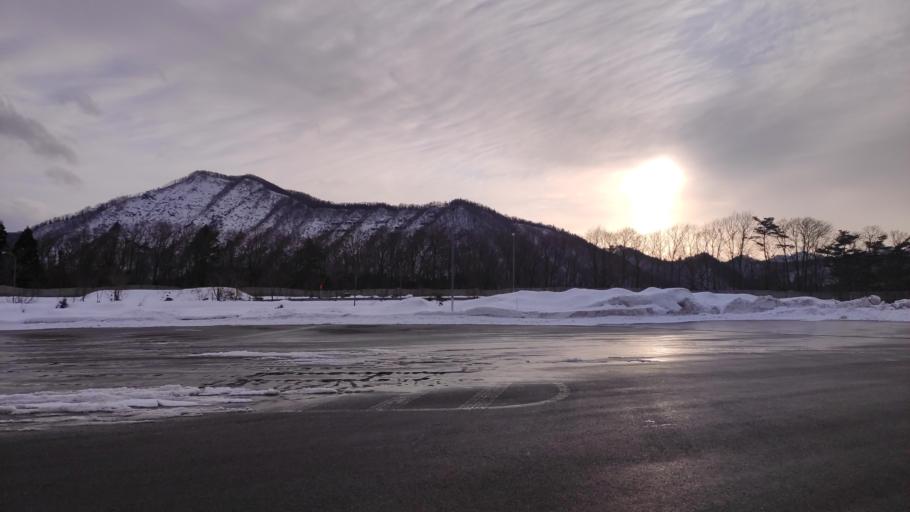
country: JP
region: Iwate
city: Kitakami
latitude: 39.2991
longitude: 140.8433
